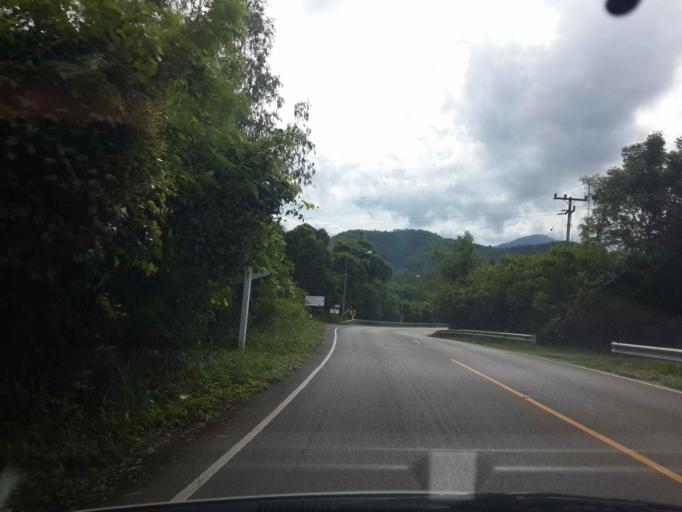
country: TH
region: Ratchaburi
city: Suan Phueng
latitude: 13.5475
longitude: 99.2813
